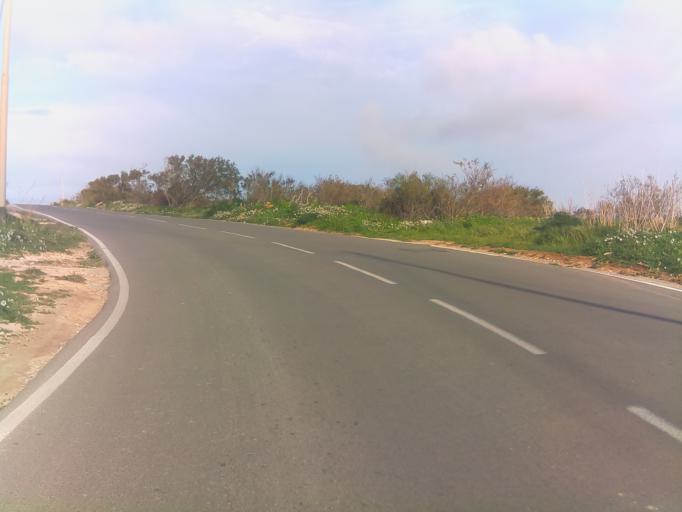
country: MT
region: Il-Mellieha
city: Mellieha
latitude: 35.9518
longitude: 14.3539
